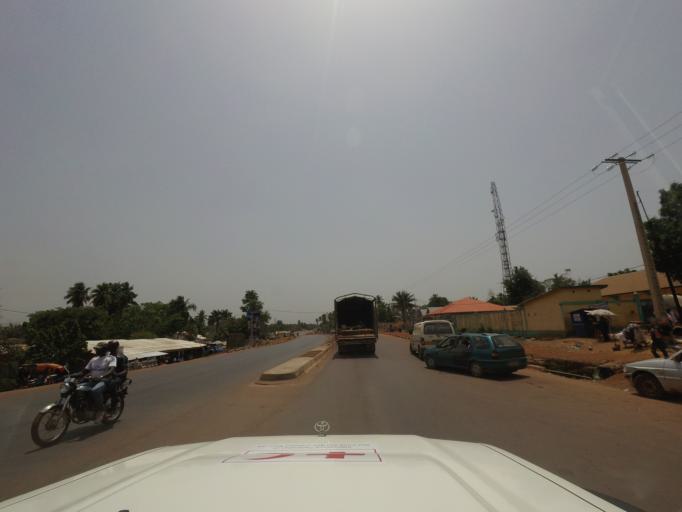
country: GN
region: Kindia
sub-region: Coyah
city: Coyah
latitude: 9.7073
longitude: -13.3928
